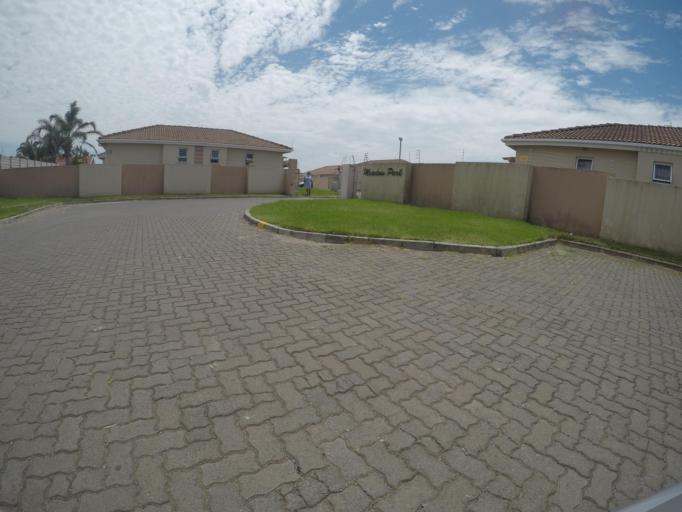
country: ZA
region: Eastern Cape
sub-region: Buffalo City Metropolitan Municipality
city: East London
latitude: -32.9834
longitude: 27.8613
